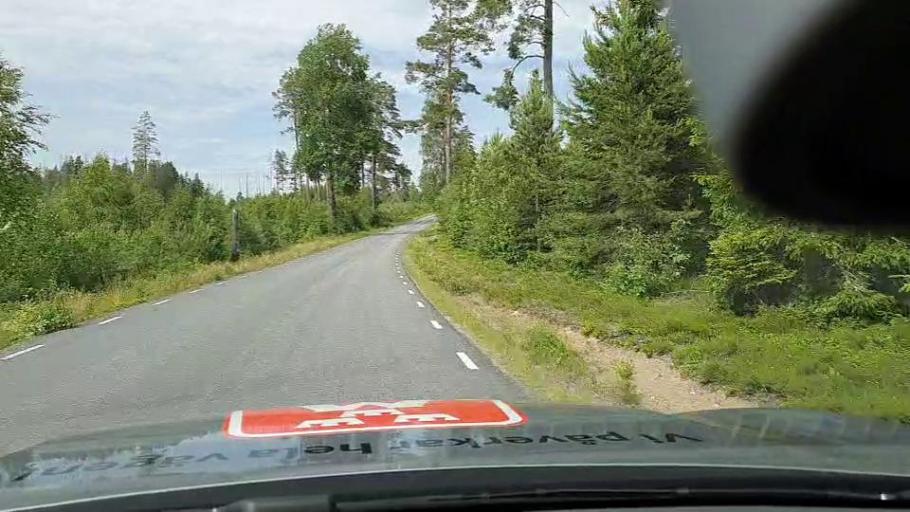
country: SE
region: Soedermanland
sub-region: Eskilstuna Kommun
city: Arla
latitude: 59.2374
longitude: 16.7224
